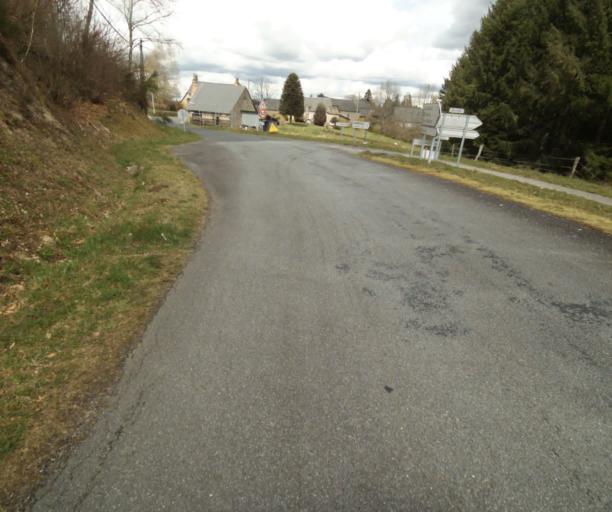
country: FR
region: Limousin
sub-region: Departement de la Correze
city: Correze
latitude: 45.3284
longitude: 1.9539
